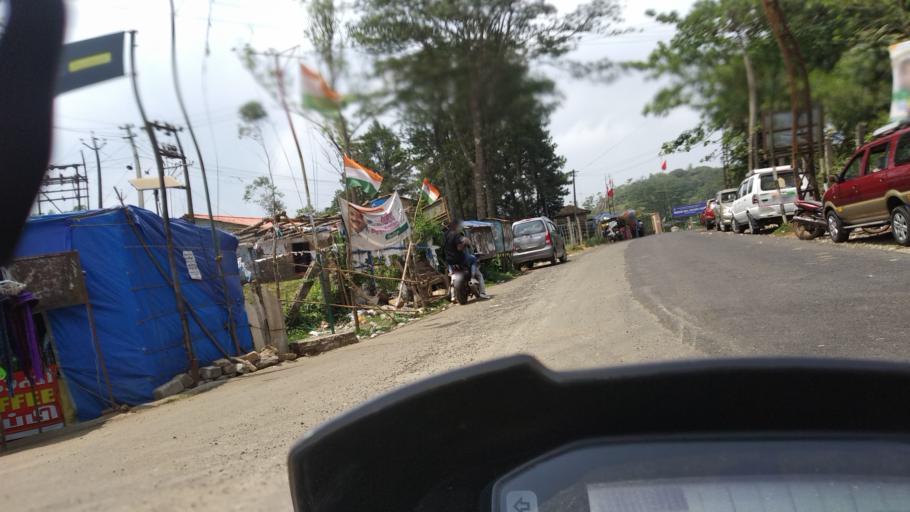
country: IN
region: Kerala
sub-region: Kottayam
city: Erattupetta
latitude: 9.6535
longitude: 76.9274
